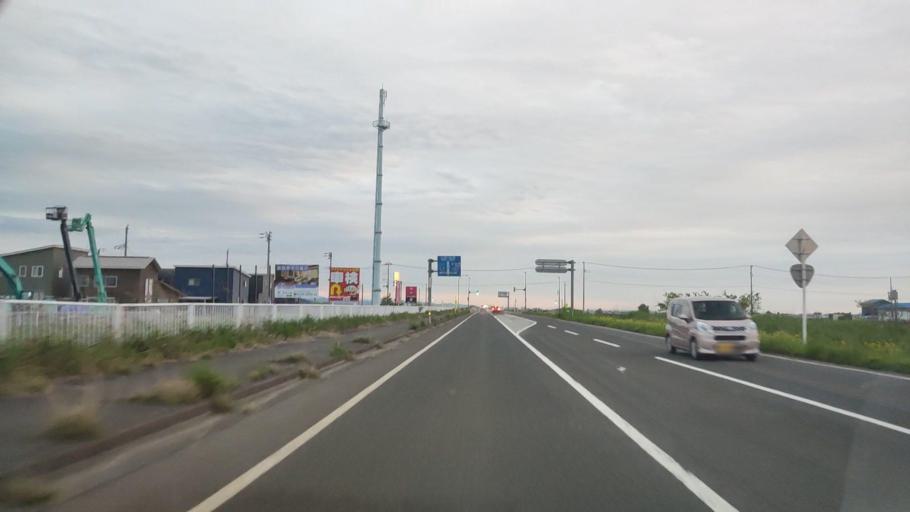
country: JP
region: Niigata
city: Niitsu-honcho
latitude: 37.7526
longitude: 139.0888
